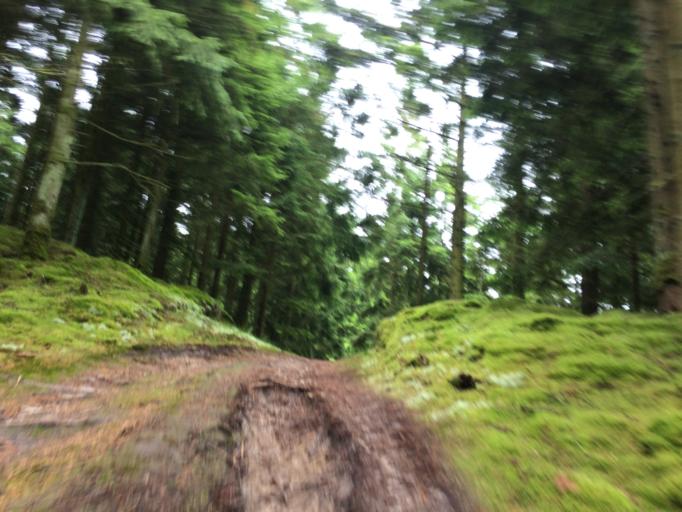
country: DK
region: Central Jutland
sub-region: Holstebro Kommune
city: Ulfborg
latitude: 56.2479
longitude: 8.4430
